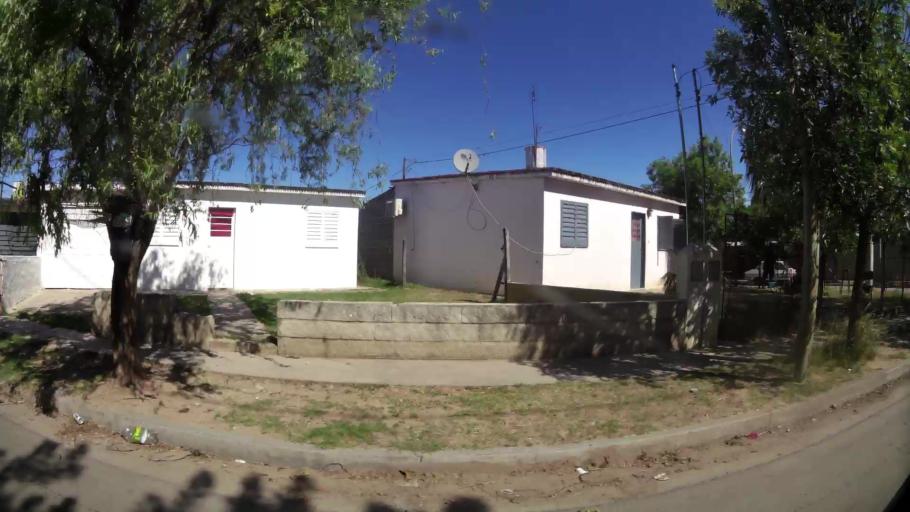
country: AR
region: Cordoba
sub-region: Departamento de Capital
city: Cordoba
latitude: -31.3624
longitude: -64.1587
